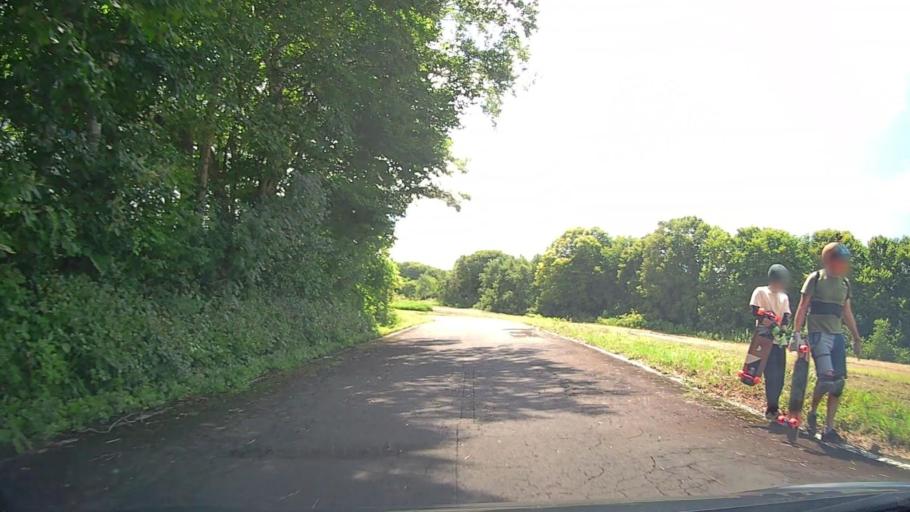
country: JP
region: Nagano
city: Iiyama
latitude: 36.9251
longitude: 138.4707
